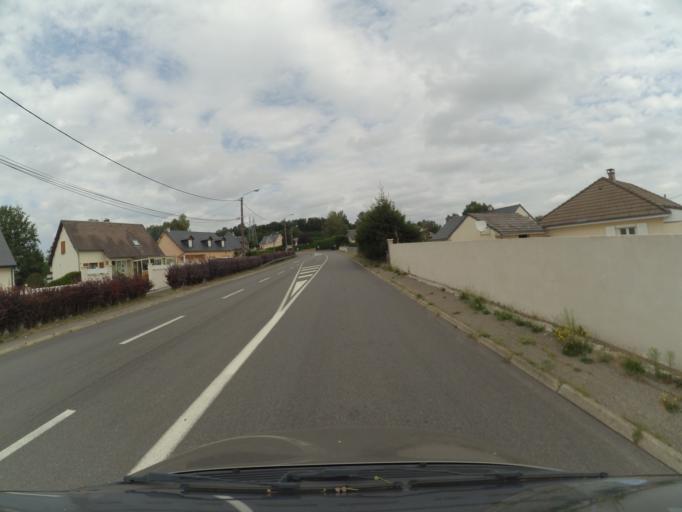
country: FR
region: Limousin
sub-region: Departement de la Correze
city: Ussel
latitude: 45.5657
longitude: 2.2995
